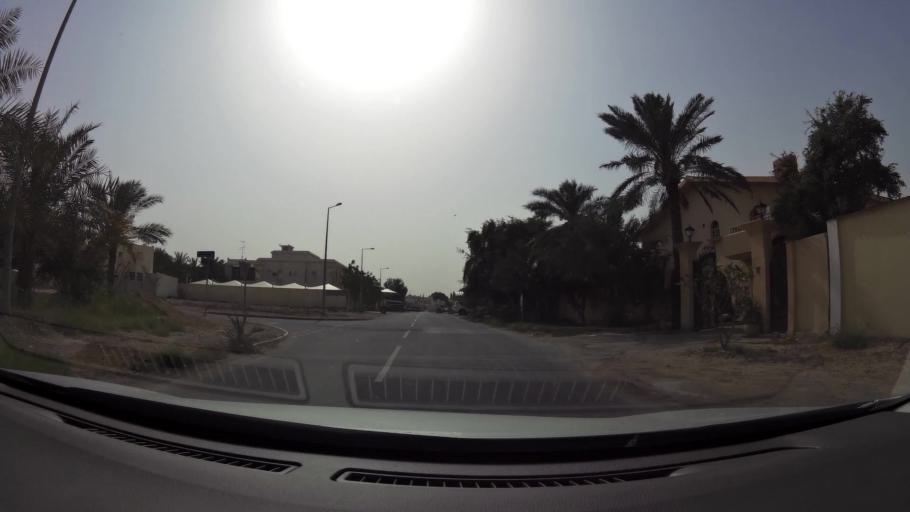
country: QA
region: Baladiyat ar Rayyan
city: Ar Rayyan
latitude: 25.2465
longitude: 51.4428
